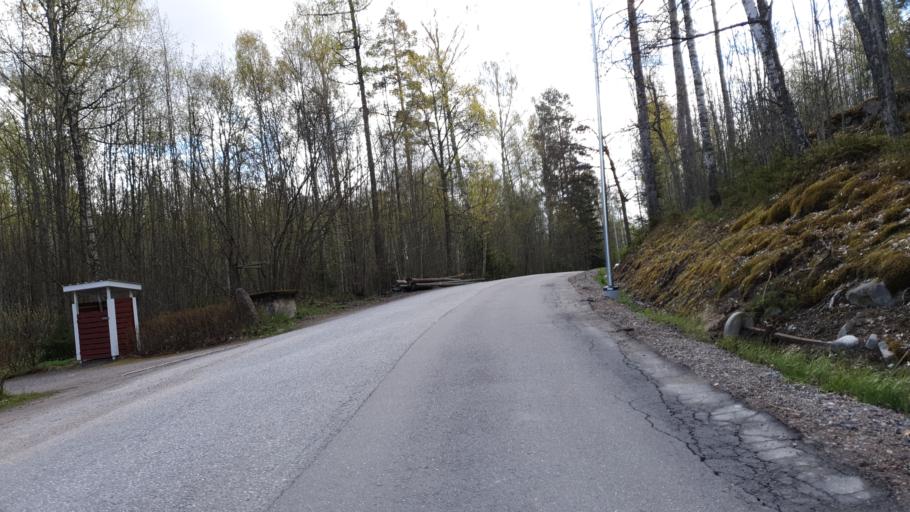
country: FI
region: Uusimaa
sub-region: Helsinki
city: Nurmijaervi
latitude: 60.3487
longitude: 24.8471
